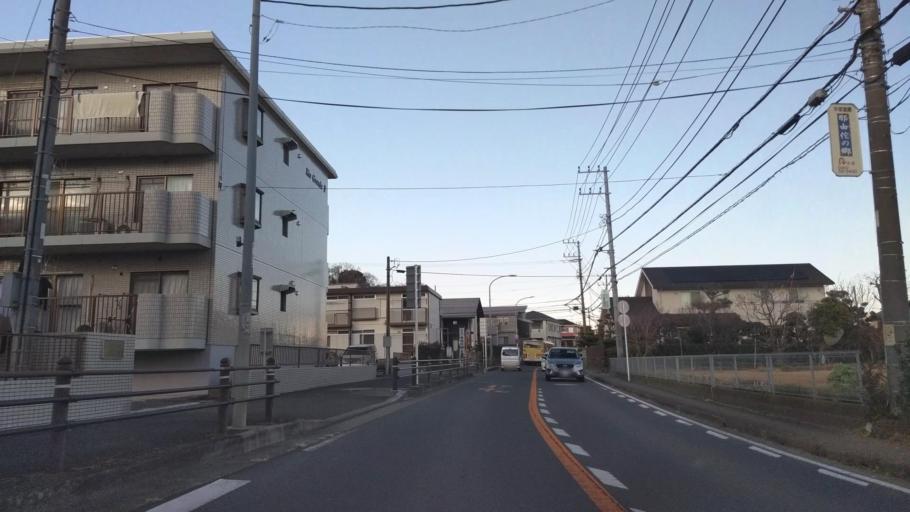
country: JP
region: Kanagawa
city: Isehara
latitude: 35.3524
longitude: 139.3015
